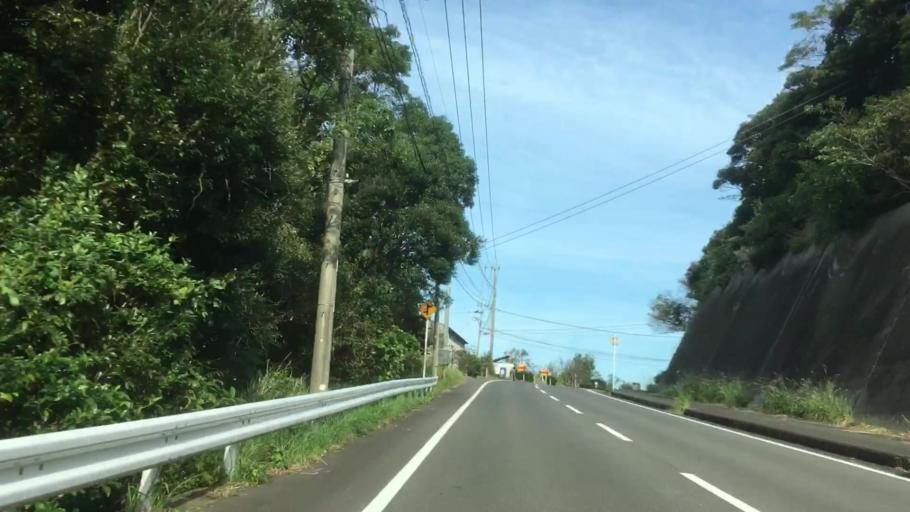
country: JP
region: Nagasaki
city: Sasebo
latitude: 33.0050
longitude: 129.6573
